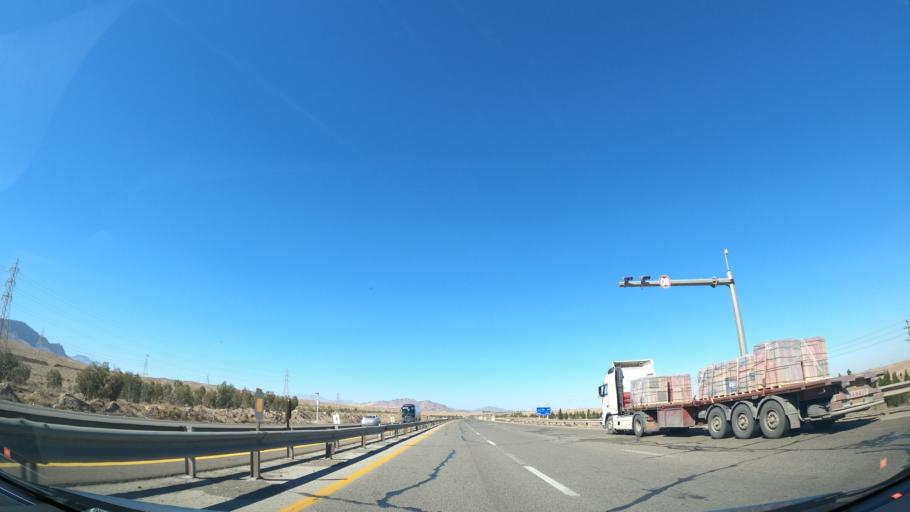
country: IR
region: Isfahan
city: Kashan
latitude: 33.9705
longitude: 51.3428
